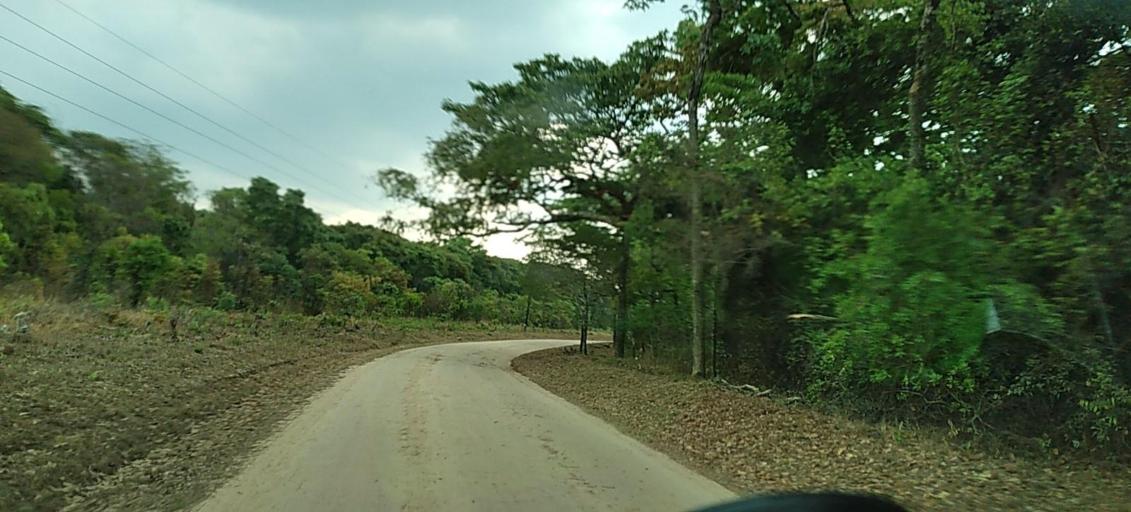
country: ZM
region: North-Western
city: Solwezi
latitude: -12.7735
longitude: 26.4688
